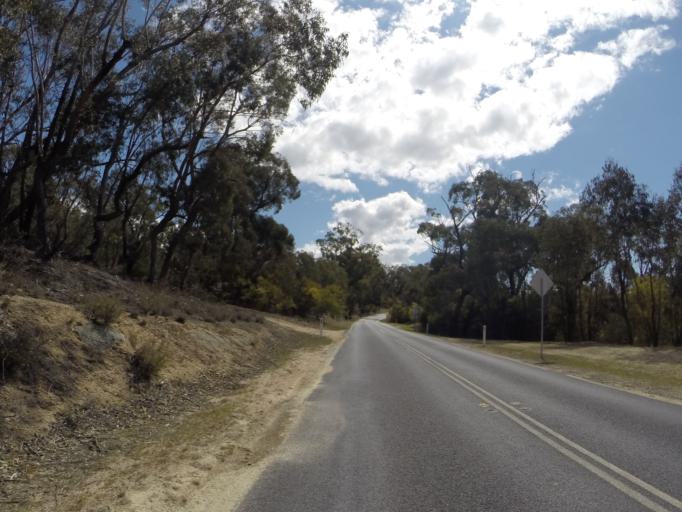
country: AU
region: Australian Capital Territory
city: Macquarie
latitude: -35.3576
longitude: 148.9458
